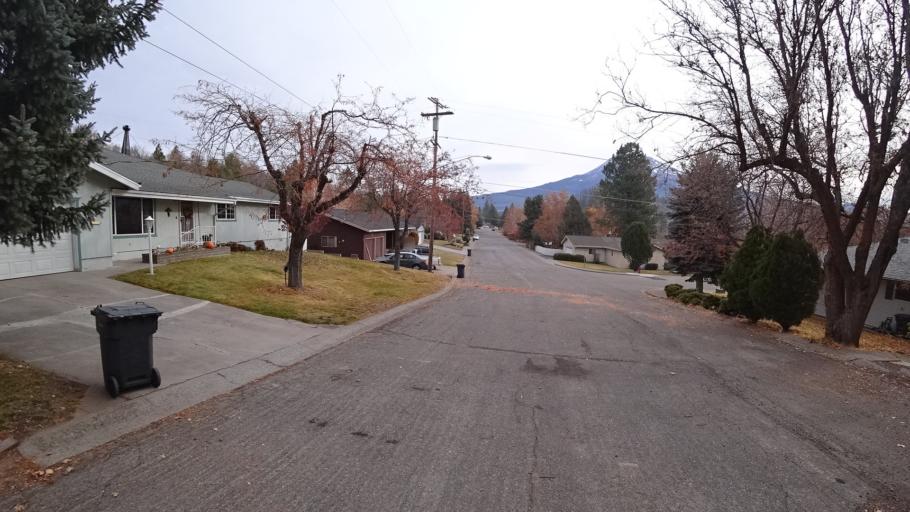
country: US
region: California
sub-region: Siskiyou County
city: Weed
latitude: 41.4170
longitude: -122.3914
